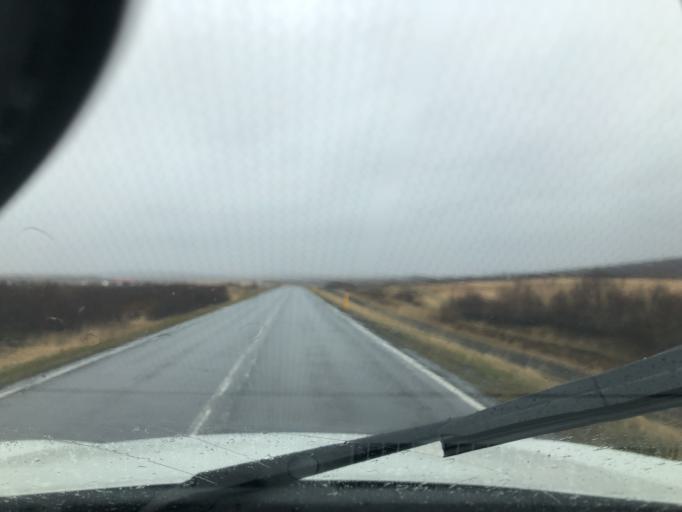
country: IS
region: South
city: Selfoss
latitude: 64.2621
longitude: -20.4709
